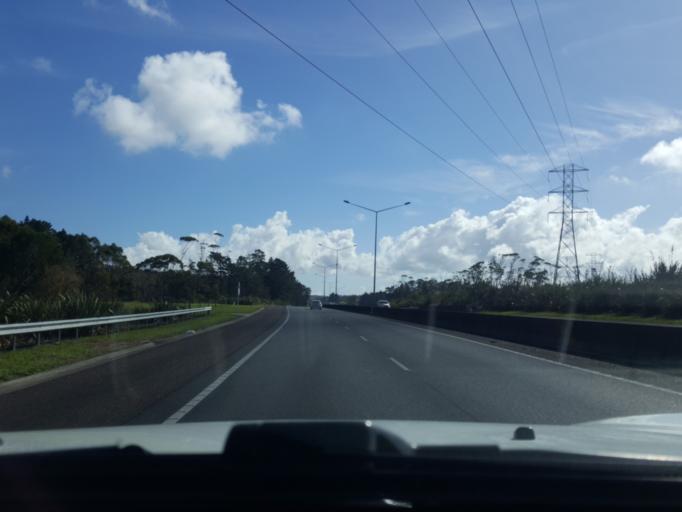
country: NZ
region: Auckland
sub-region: Auckland
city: Rosebank
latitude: -36.8062
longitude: 174.6066
